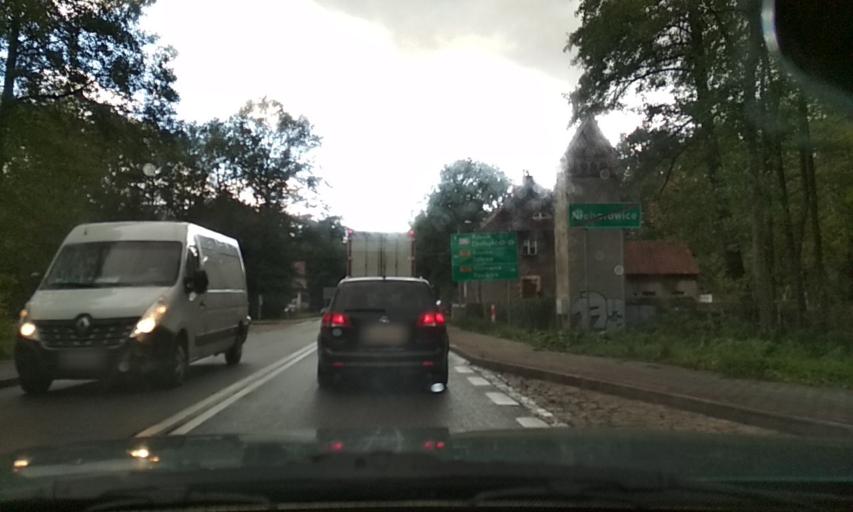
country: PL
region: Silesian Voivodeship
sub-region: Powiat gliwicki
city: Wilcza
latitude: 50.2160
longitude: 18.6013
